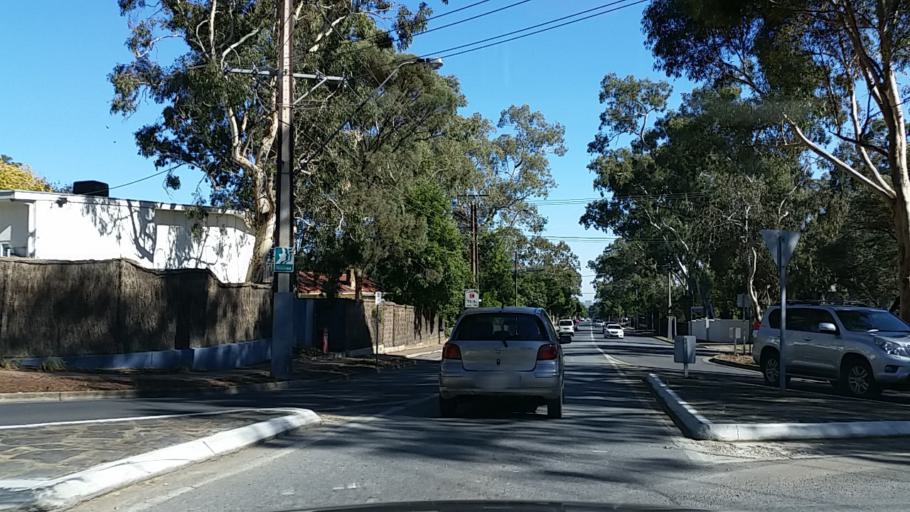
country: AU
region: South Australia
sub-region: Burnside
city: Kensington Gardens
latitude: -34.9255
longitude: 138.6680
